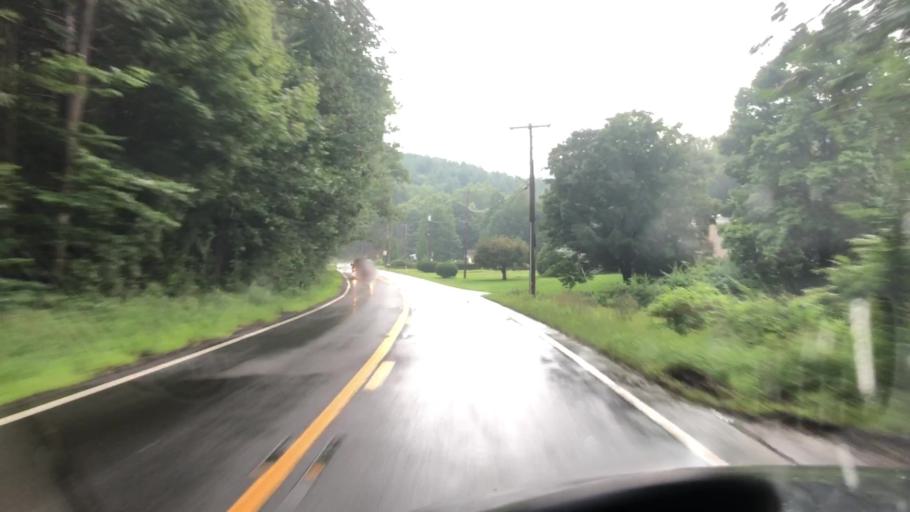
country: US
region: Massachusetts
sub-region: Hampshire County
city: Westhampton
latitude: 42.2633
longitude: -72.8648
